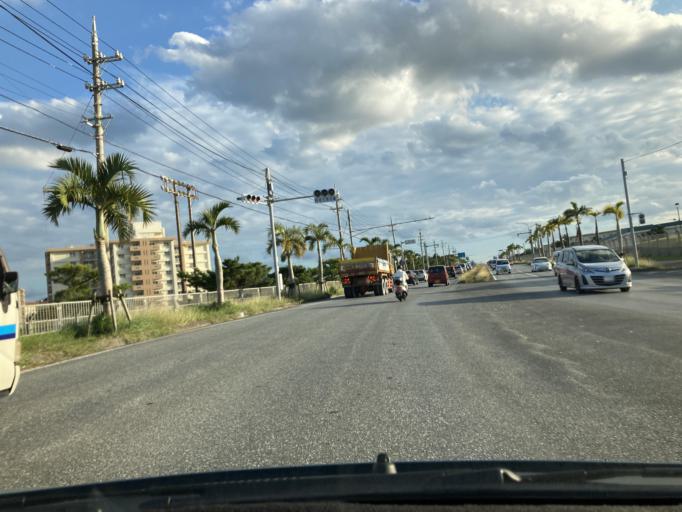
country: JP
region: Okinawa
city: Chatan
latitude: 26.3016
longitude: 127.7804
